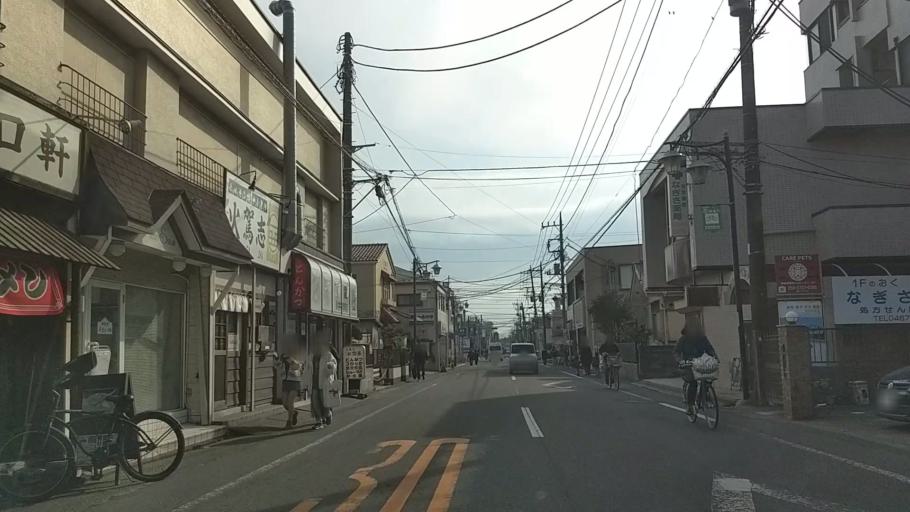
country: JP
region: Kanagawa
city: Chigasaki
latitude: 35.3260
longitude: 139.4083
